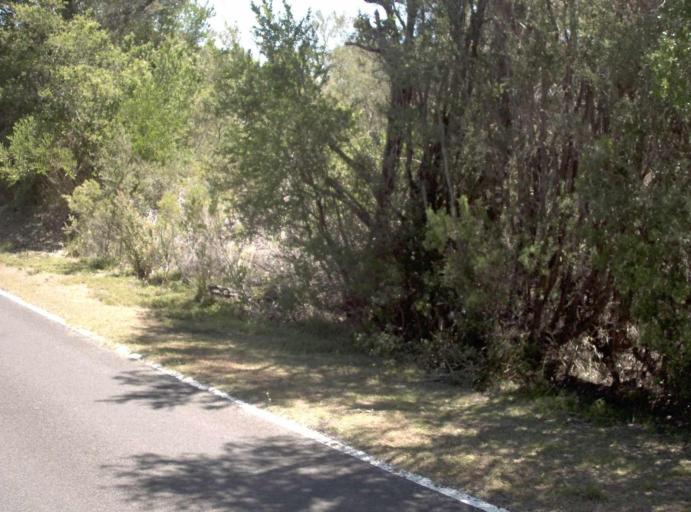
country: AU
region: Victoria
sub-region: Latrobe
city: Morwell
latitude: -38.8782
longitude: 146.2655
